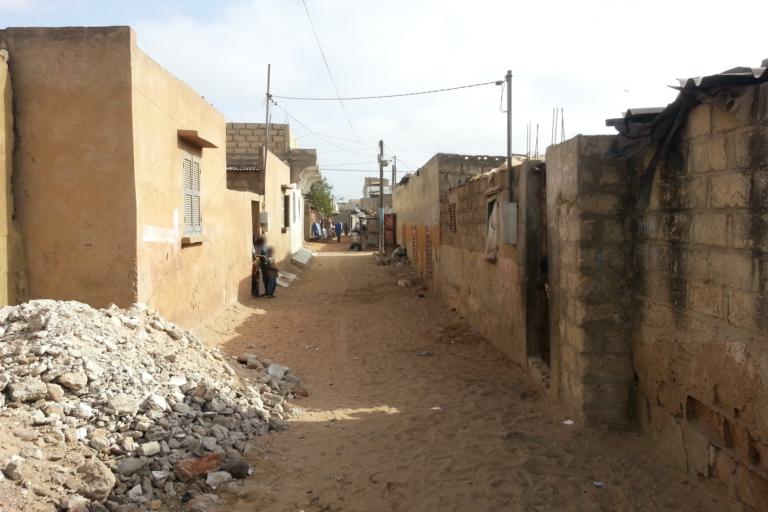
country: SN
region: Dakar
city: Pikine
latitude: 14.7701
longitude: -17.3864
